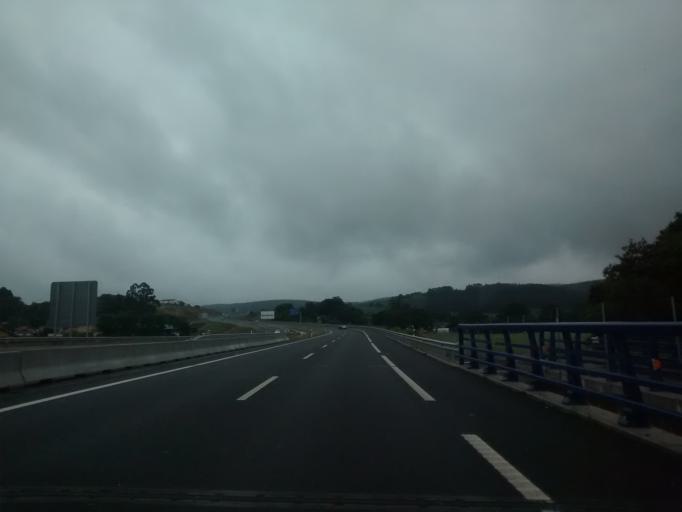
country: ES
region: Cantabria
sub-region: Provincia de Cantabria
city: Puente Viesgo
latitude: 43.3357
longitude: -3.9832
